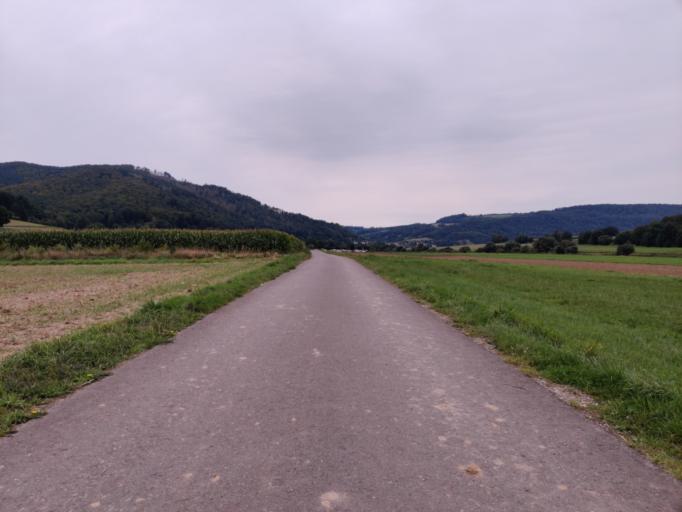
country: DE
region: Lower Saxony
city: Pegestorf
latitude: 51.9490
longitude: 9.5064
